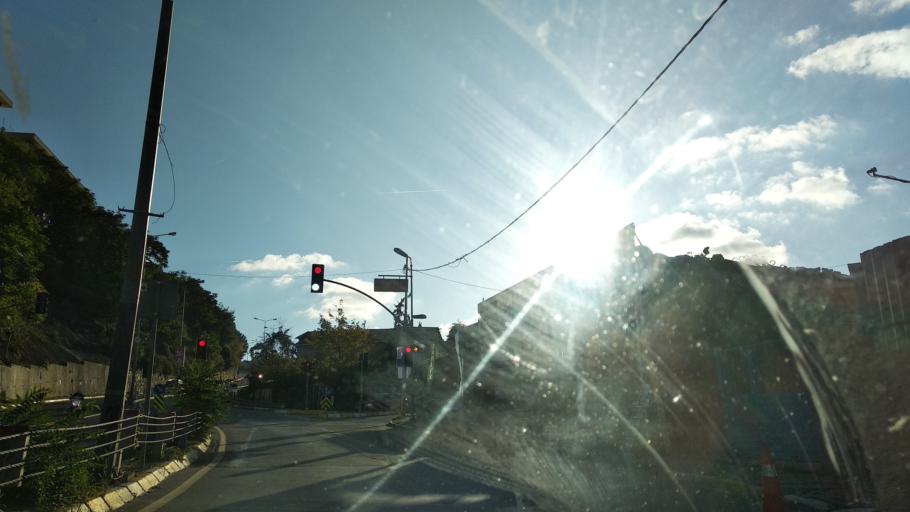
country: TR
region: Istanbul
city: Sisli
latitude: 41.1279
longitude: 29.0345
